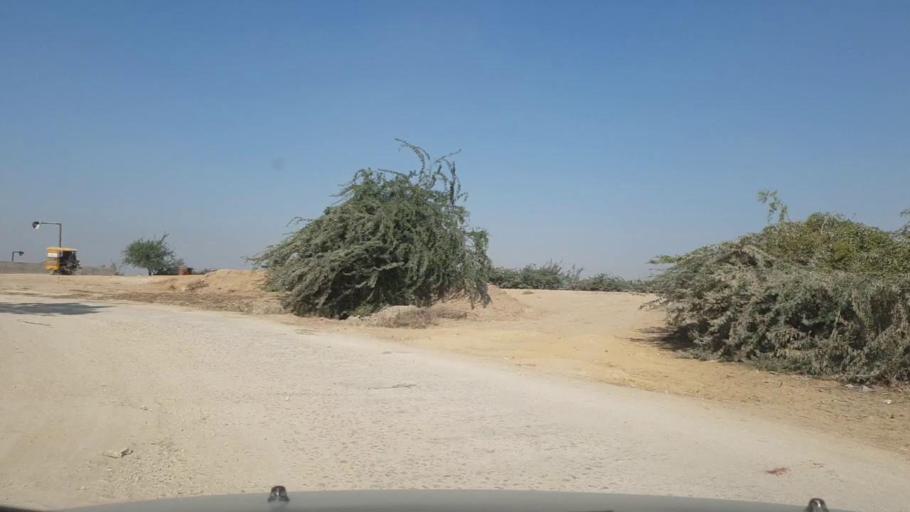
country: PK
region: Sindh
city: Thatta
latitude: 24.8022
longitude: 67.9020
